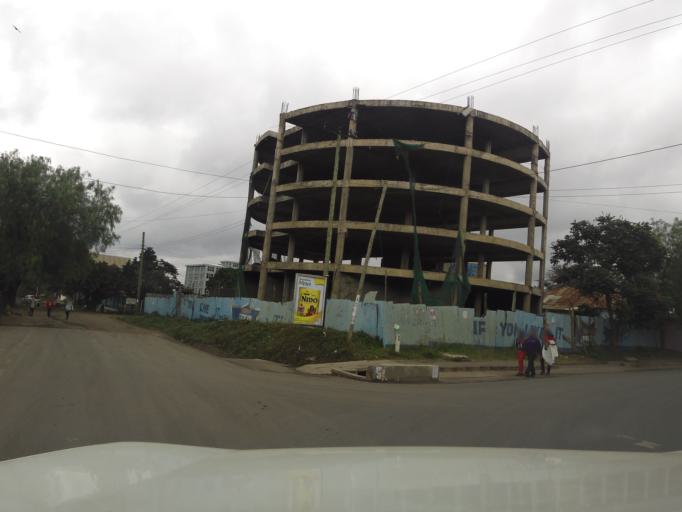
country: TZ
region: Arusha
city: Arusha
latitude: -3.3651
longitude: 36.6877
